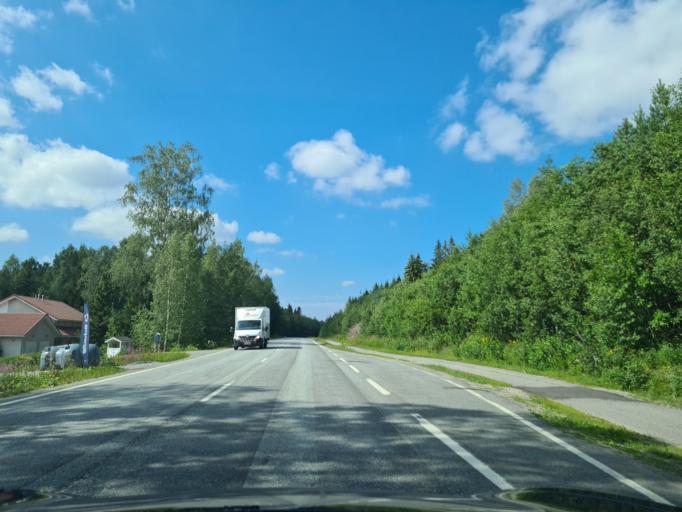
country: FI
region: Ostrobothnia
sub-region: Vaasa
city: Vaasa
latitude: 63.1980
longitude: 21.5405
